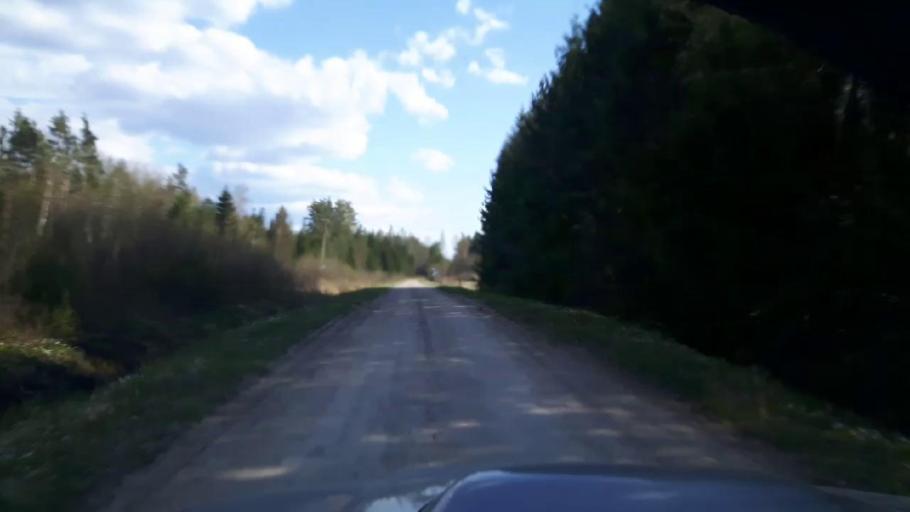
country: EE
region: Paernumaa
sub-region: Tootsi vald
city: Tootsi
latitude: 58.4285
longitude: 24.8513
